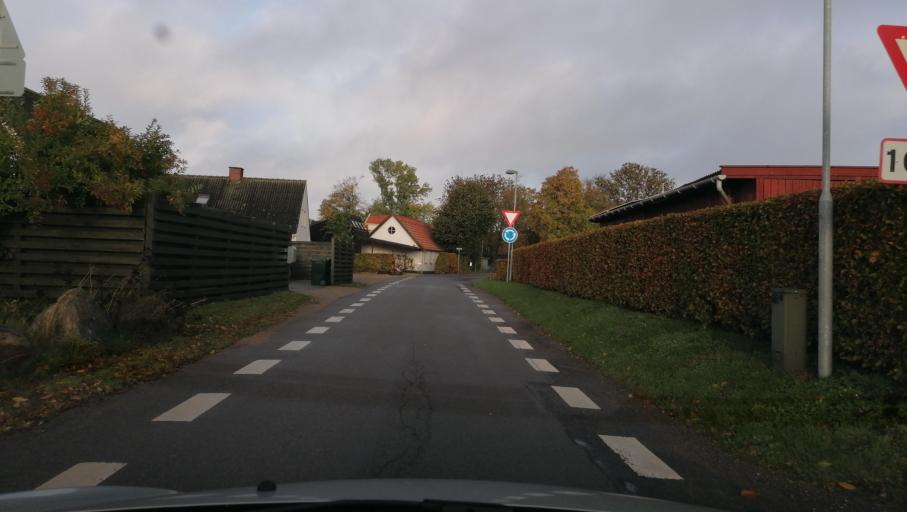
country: DK
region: Zealand
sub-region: Odsherred Kommune
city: Horve
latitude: 55.7392
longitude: 11.4005
